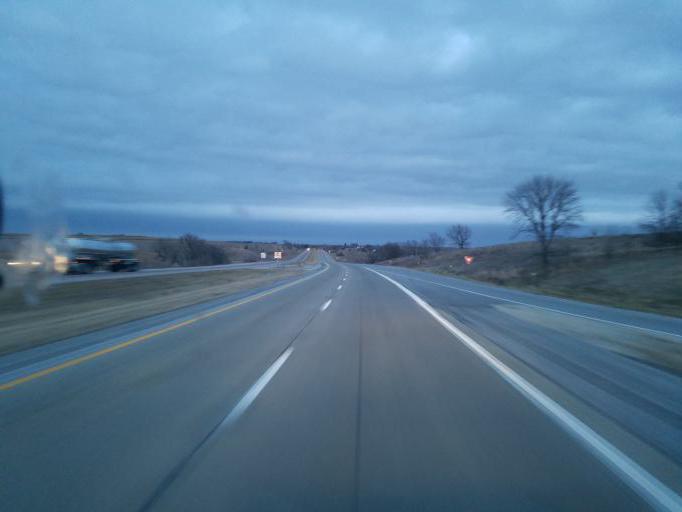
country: US
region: Iowa
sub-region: Cass County
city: Atlantic
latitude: 41.4969
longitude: -95.1142
